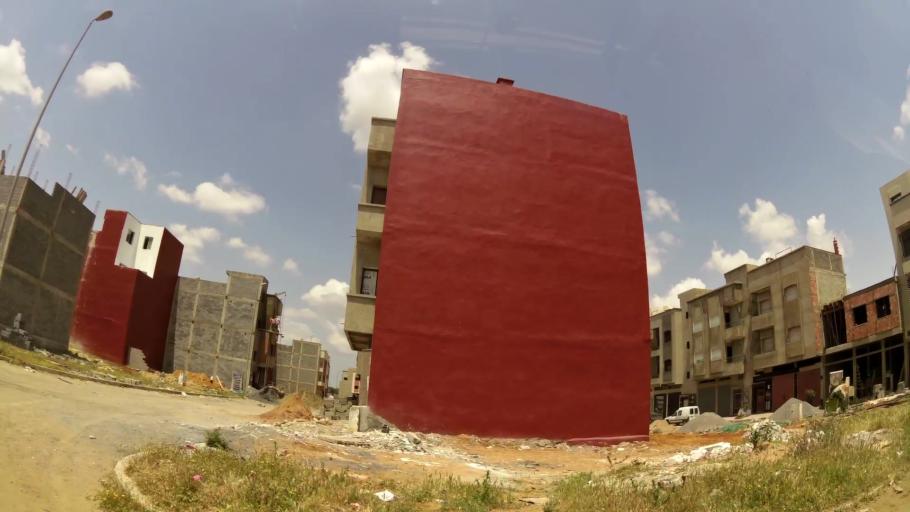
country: MA
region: Rabat-Sale-Zemmour-Zaer
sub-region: Khemisset
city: Tiflet
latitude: 34.0116
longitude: -6.5255
